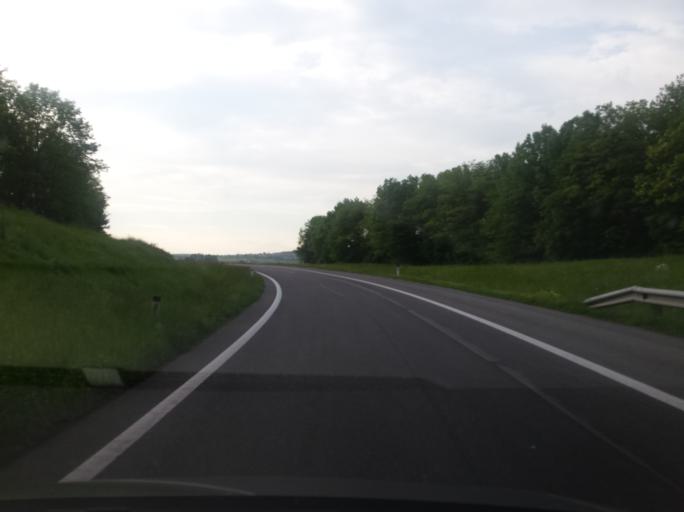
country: AT
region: Burgenland
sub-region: Eisenstadt-Umgebung
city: Wulkaprodersdorf
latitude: 47.8165
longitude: 16.4984
